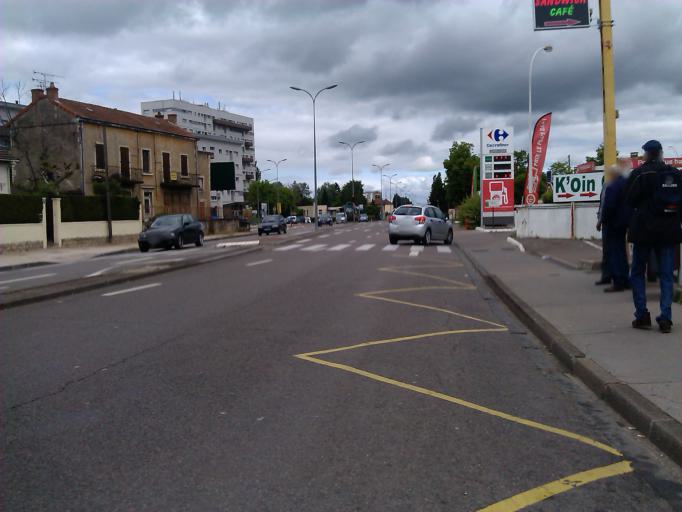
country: FR
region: Bourgogne
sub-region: Departement de Saone-et-Loire
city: Chalon-sur-Saone
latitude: 46.7976
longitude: 4.8477
